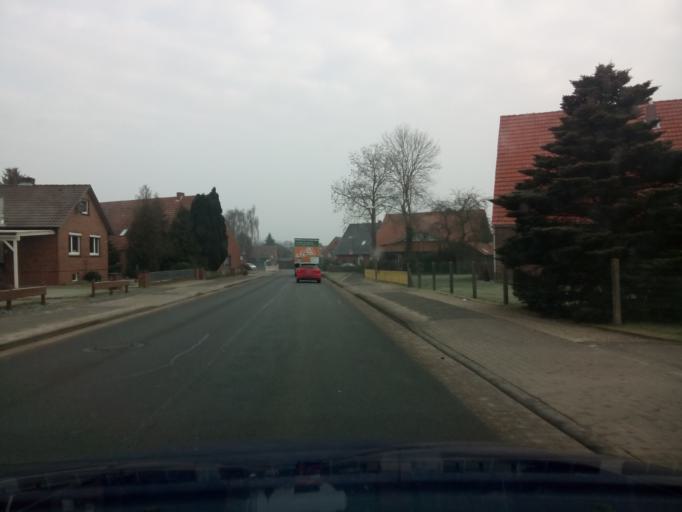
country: DE
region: Lower Saxony
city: Elmlohe
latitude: 53.6057
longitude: 8.6762
